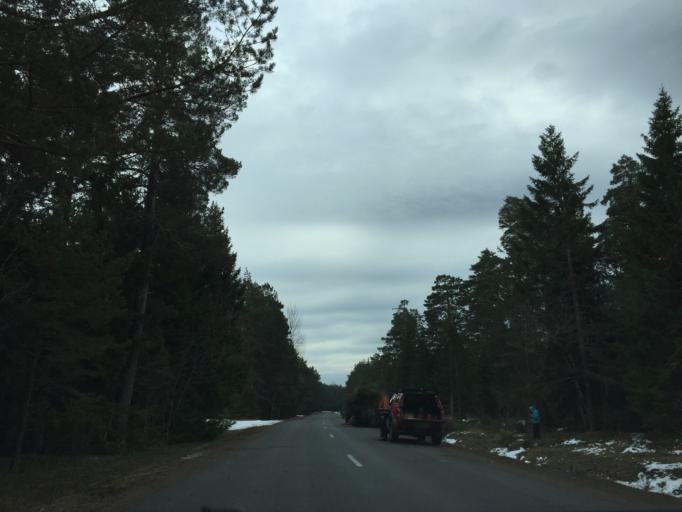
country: EE
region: Saare
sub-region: Kuressaare linn
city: Kuressaare
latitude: 58.4293
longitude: 22.0715
